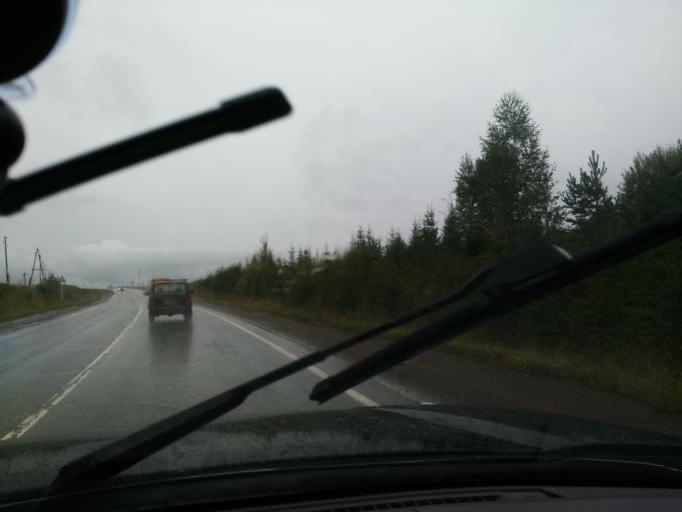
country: RU
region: Perm
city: Yugo-Kamskiy
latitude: 57.6967
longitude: 55.6162
